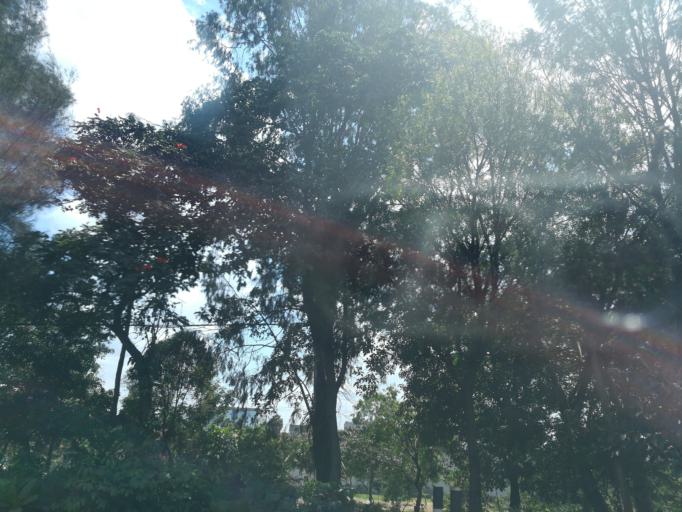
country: KE
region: Nairobi Area
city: Nairobi
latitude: -1.3129
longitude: 36.8147
